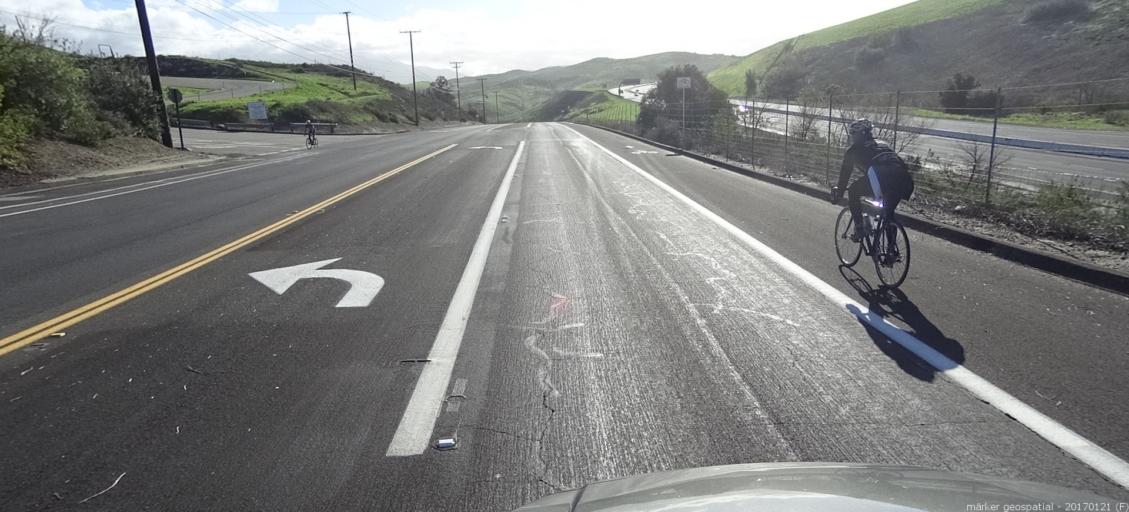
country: US
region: California
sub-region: Orange County
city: North Tustin
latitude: 33.7712
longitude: -117.7394
